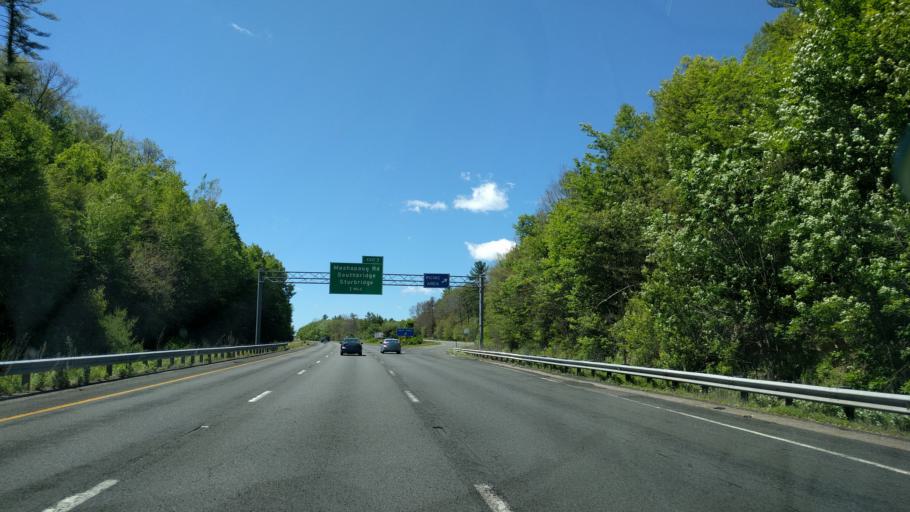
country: US
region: Massachusetts
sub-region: Worcester County
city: Sturbridge
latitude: 42.0856
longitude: -72.0958
